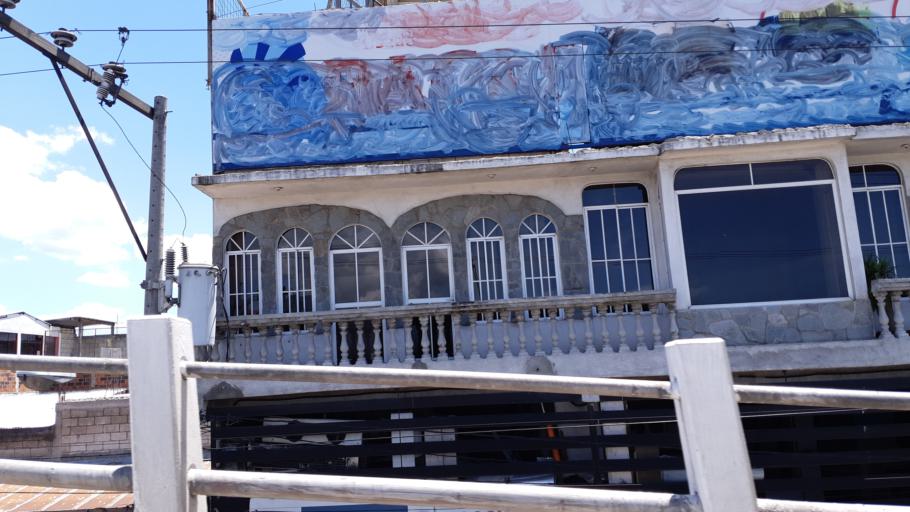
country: GT
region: Chimaltenango
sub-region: Municipio de Chimaltenango
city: Chimaltenango
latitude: 14.6583
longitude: -90.8141
